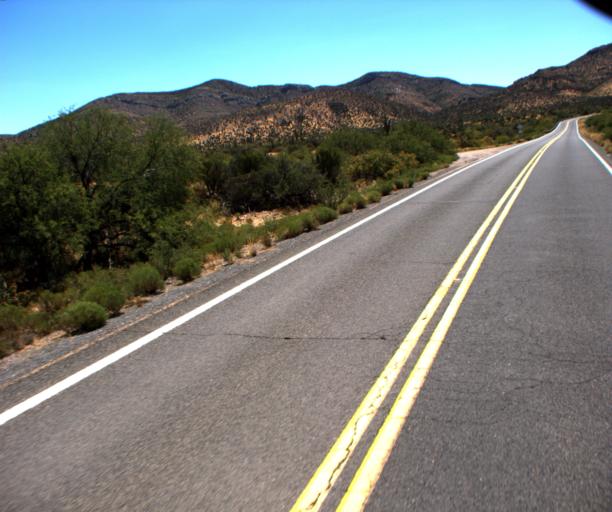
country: US
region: Arizona
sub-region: Pinal County
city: Superior
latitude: 33.2204
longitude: -111.0699
